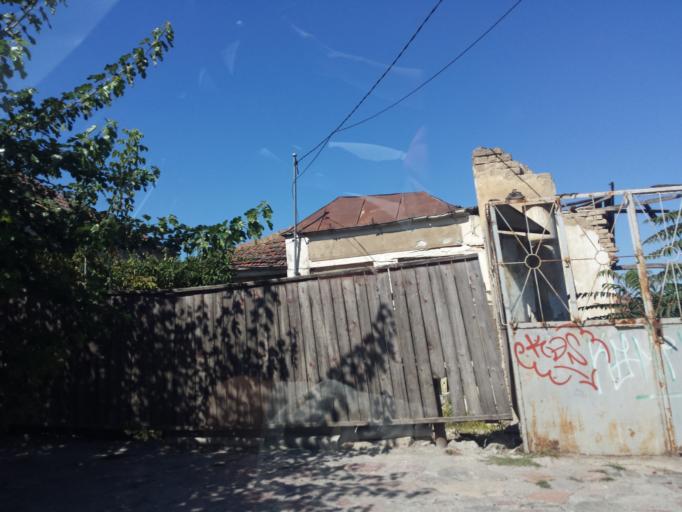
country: RO
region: Tulcea
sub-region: Municipiul Tulcea
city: Tulcea
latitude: 45.1829
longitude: 28.8101
